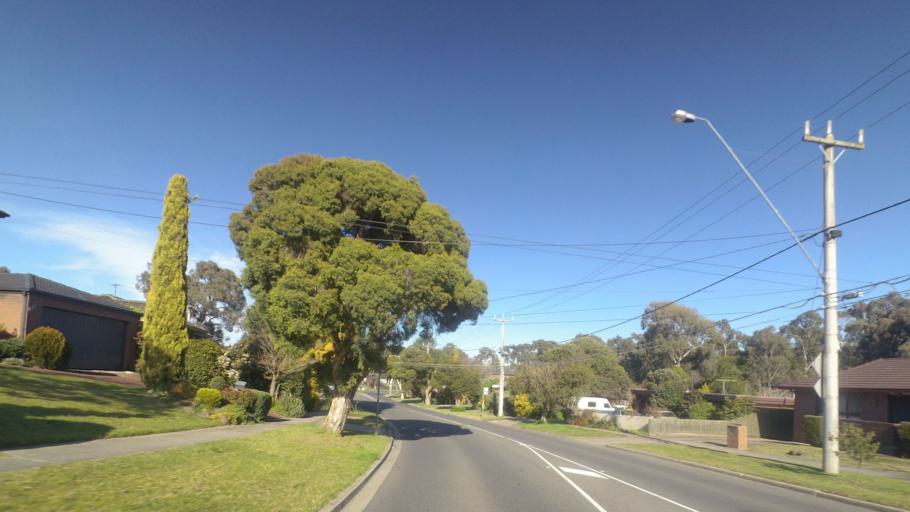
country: AU
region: Victoria
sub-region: Banyule
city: Yallambie
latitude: -37.7280
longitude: 145.1020
